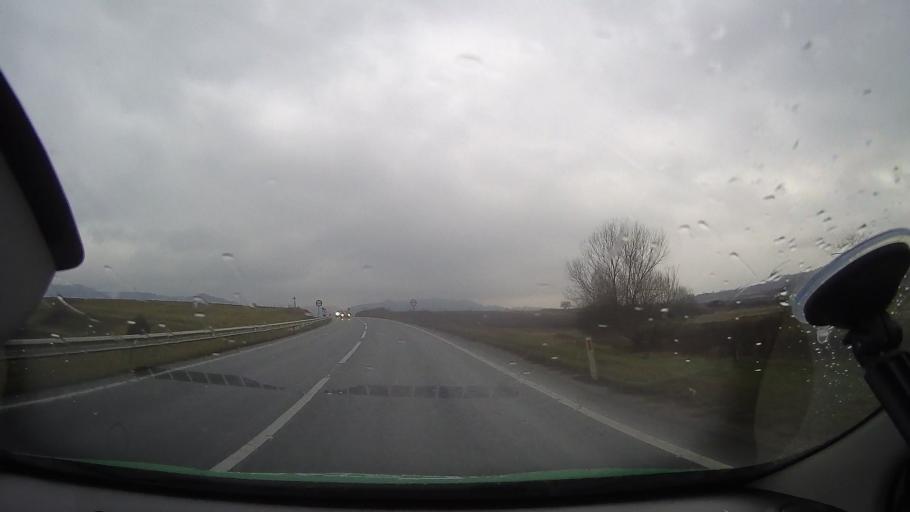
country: RO
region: Hunedoara
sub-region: Comuna Baia de Cris
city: Baia de Cris
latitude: 46.1682
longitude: 22.7398
